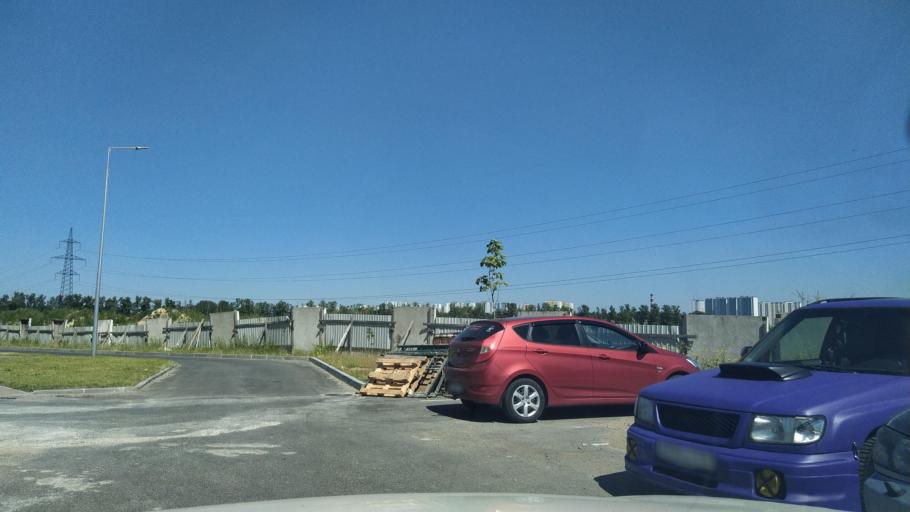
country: RU
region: St.-Petersburg
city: Krasnogvargeisky
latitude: 60.0000
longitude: 30.4539
